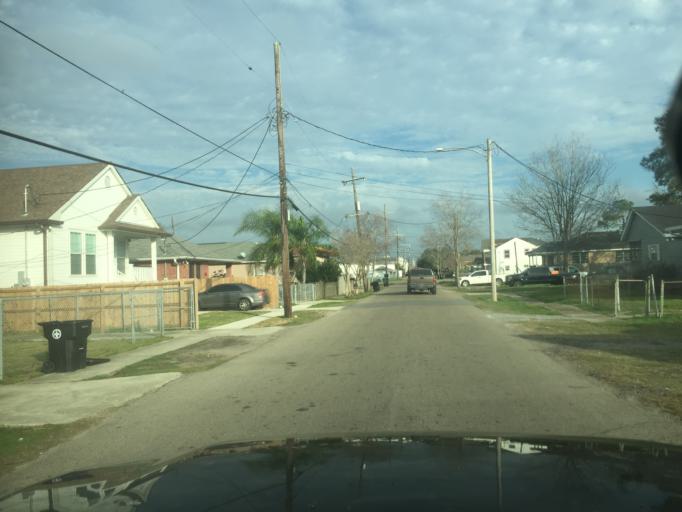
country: US
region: Louisiana
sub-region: Orleans Parish
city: New Orleans
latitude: 29.9946
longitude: -90.0816
